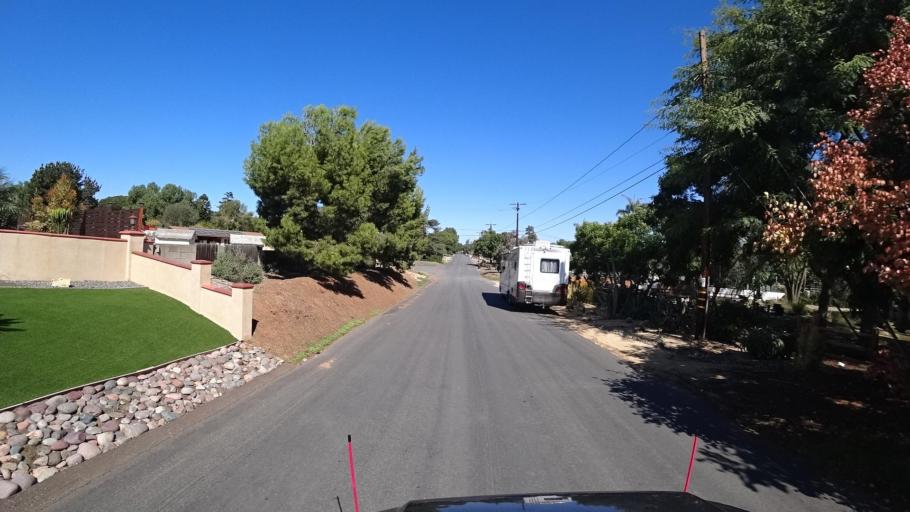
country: US
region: California
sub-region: San Diego County
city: Bonita
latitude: 32.6528
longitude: -117.0557
